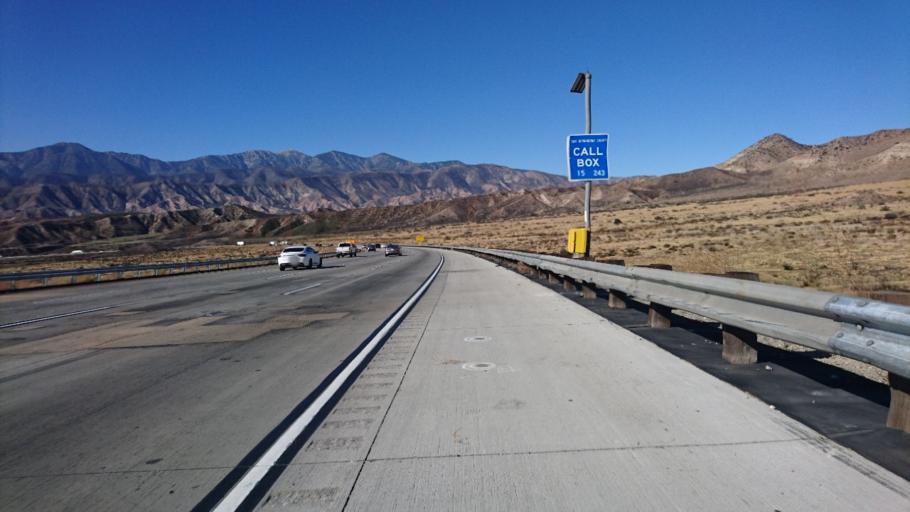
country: US
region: California
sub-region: San Bernardino County
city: Oak Hills
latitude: 34.3480
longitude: -117.4734
